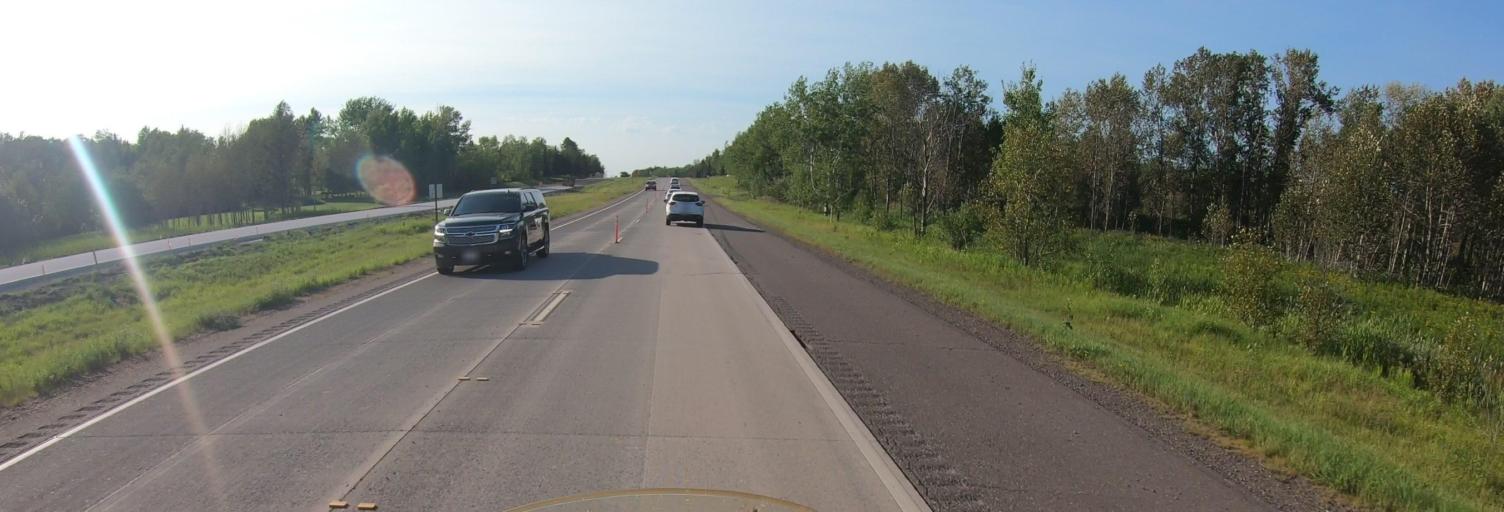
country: US
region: Minnesota
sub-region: Carlton County
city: Cloquet
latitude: 46.9252
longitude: -92.4140
